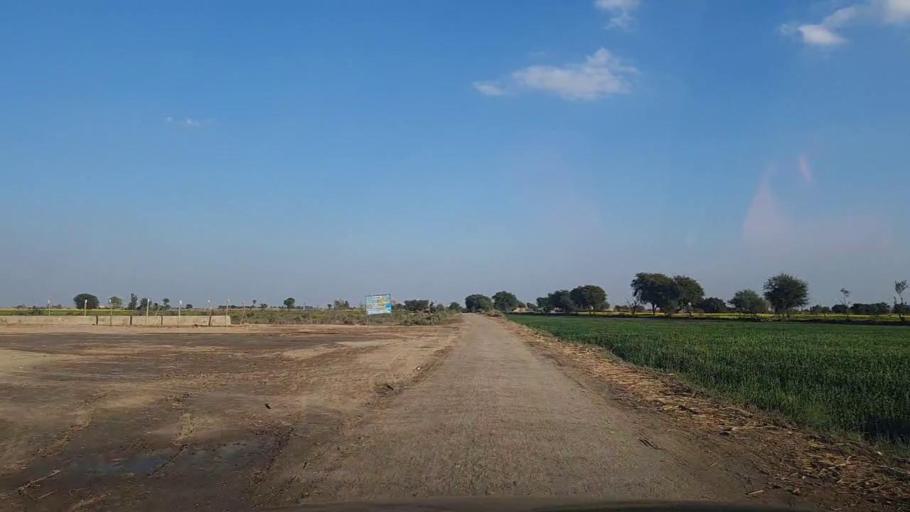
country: PK
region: Sindh
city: Jhol
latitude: 25.9218
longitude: 69.0333
